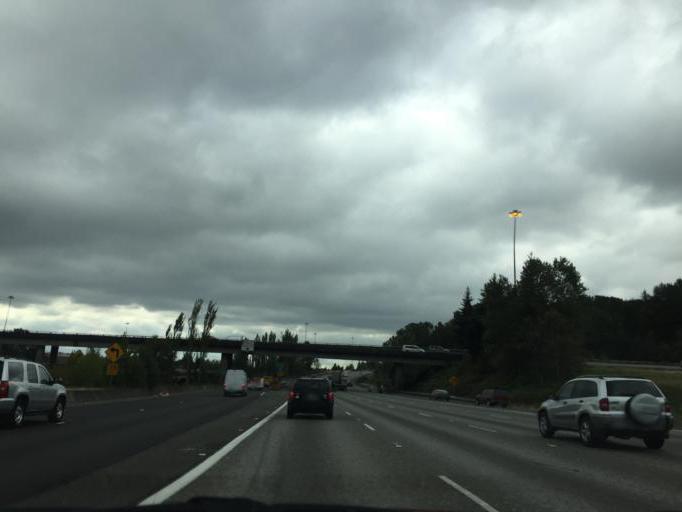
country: US
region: Washington
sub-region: King County
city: Tukwila
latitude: 47.4639
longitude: -122.2663
